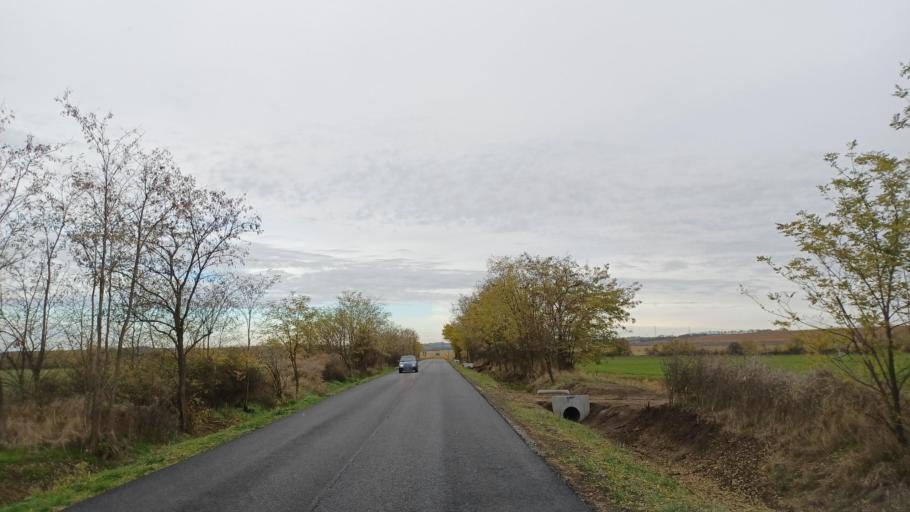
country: HU
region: Tolna
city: Tengelic
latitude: 46.5476
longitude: 18.7517
